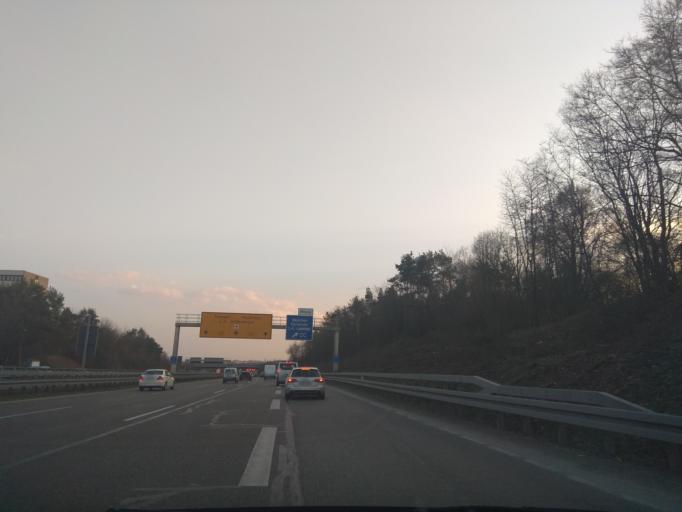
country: DE
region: Baden-Wuerttemberg
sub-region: Regierungsbezirk Stuttgart
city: Leinfelden-Echterdingen
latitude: 48.7116
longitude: 9.1641
